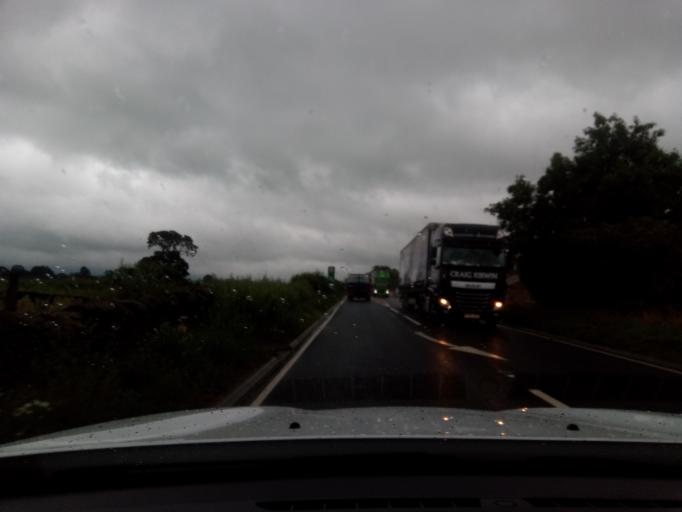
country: GB
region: England
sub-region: Cumbria
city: Appleby-in-Westmorland
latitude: 54.6264
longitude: -2.5774
